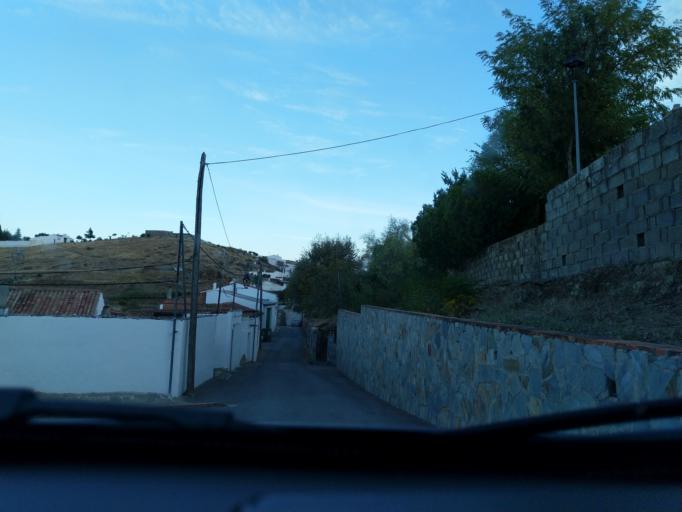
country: ES
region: Extremadura
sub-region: Provincia de Badajoz
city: Reina
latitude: 38.1889
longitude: -5.9514
